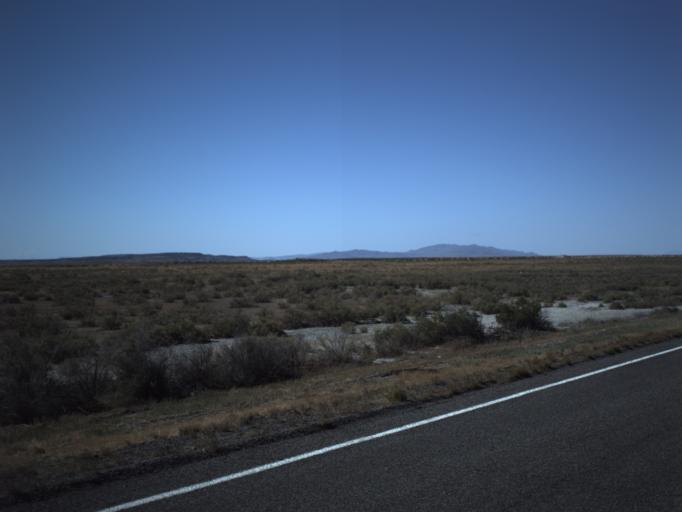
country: US
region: Utah
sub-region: Millard County
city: Delta
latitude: 39.3228
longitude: -112.7363
